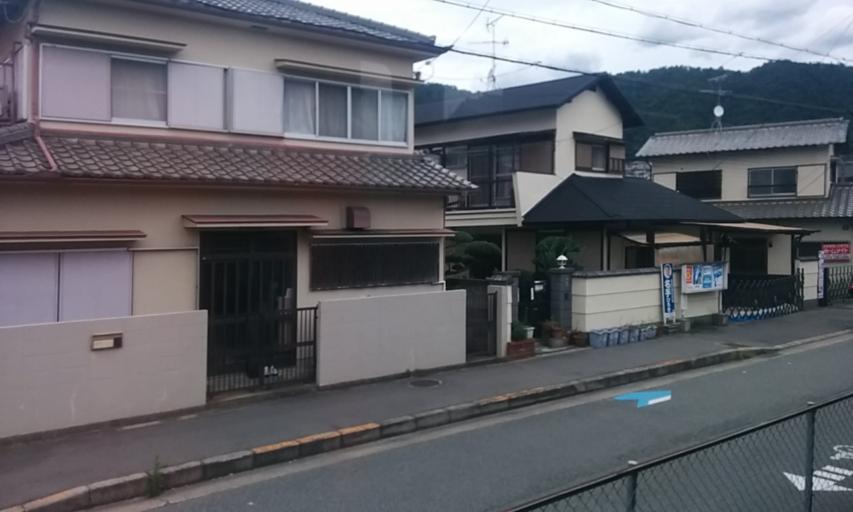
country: JP
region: Osaka
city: Mino
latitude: 34.8306
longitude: 135.4673
